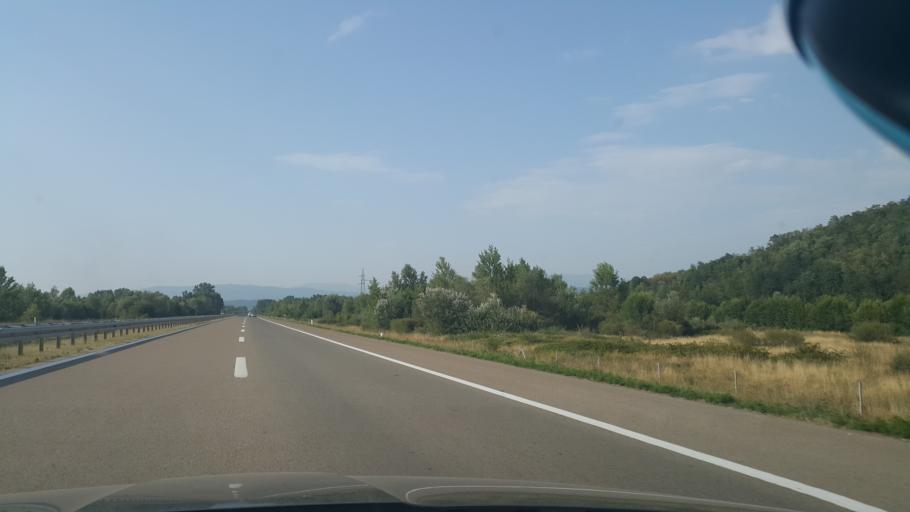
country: RS
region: Central Serbia
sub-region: Jablanicki Okrug
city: Leskovac
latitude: 42.9320
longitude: 22.0298
